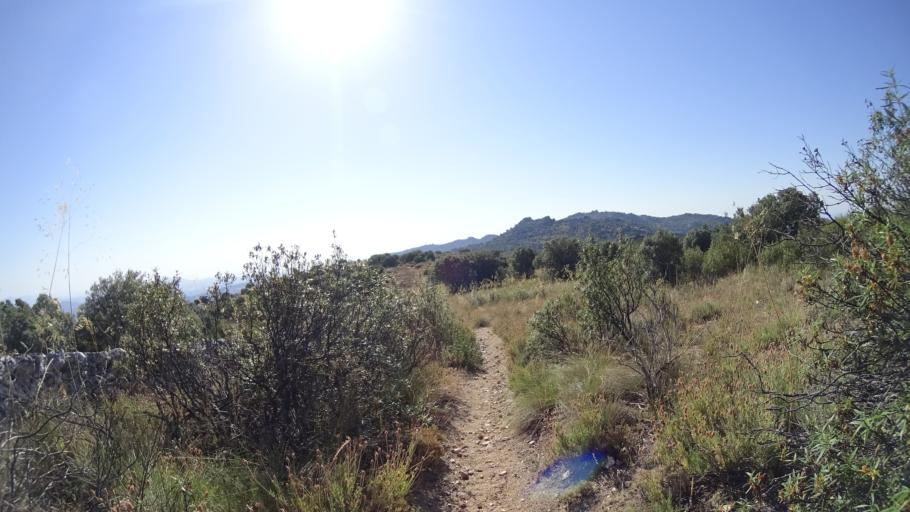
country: ES
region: Madrid
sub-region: Provincia de Madrid
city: Moralzarzal
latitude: 40.6497
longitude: -3.9397
